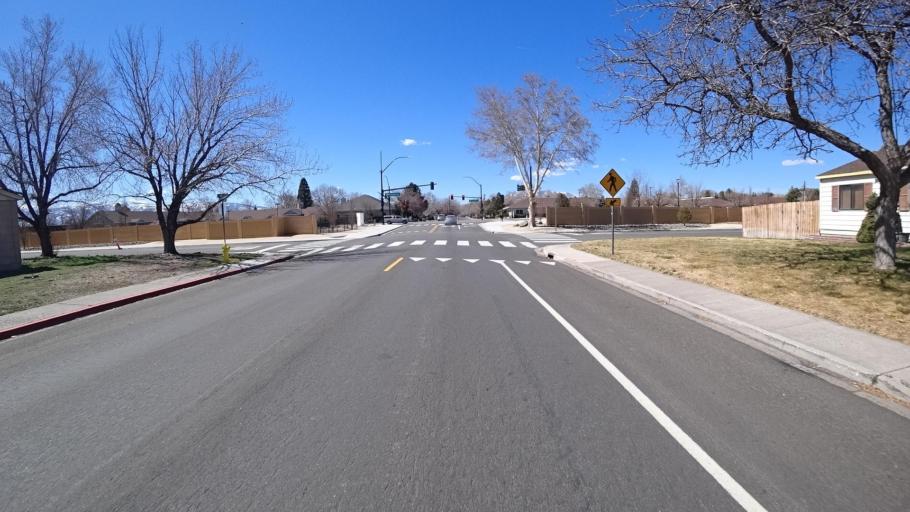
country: US
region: Nevada
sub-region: Washoe County
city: Sparks
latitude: 39.5528
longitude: -119.7516
